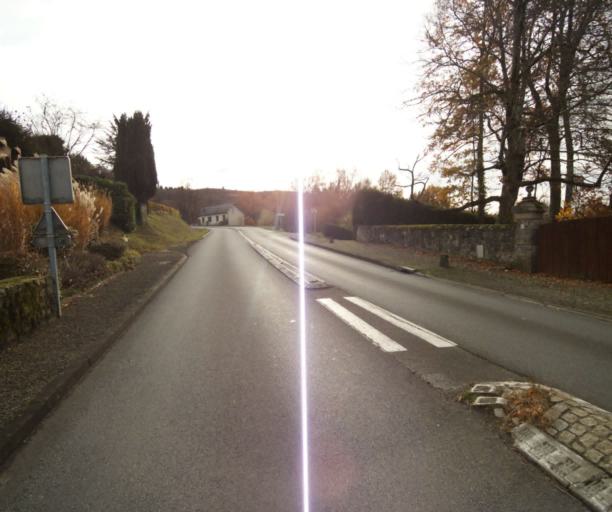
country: FR
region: Limousin
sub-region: Departement de la Correze
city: Sainte-Fortunade
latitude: 45.2032
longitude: 1.7711
